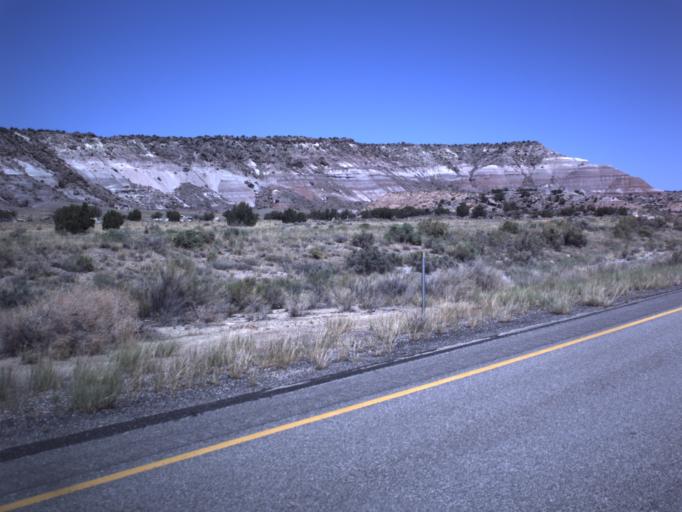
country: US
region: Utah
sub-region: Emery County
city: Ferron
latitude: 38.8197
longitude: -111.1540
